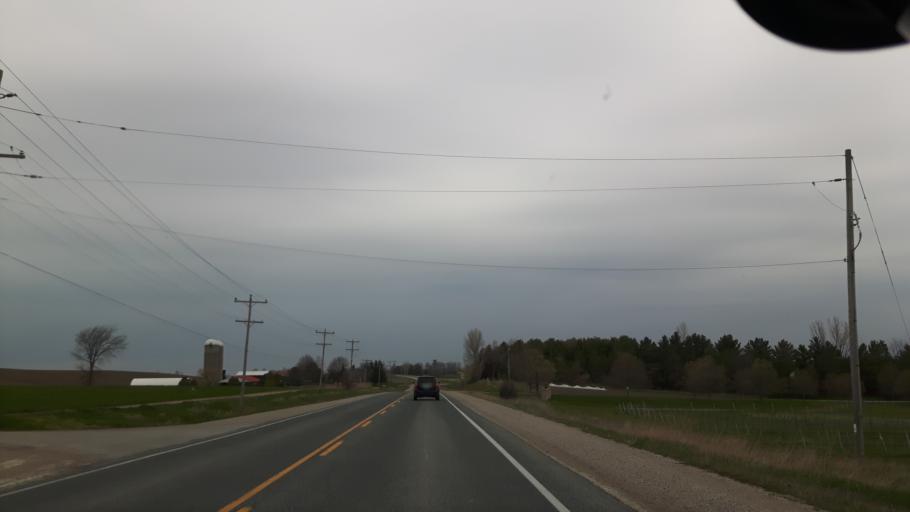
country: CA
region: Ontario
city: Goderich
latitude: 43.6842
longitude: -81.6301
